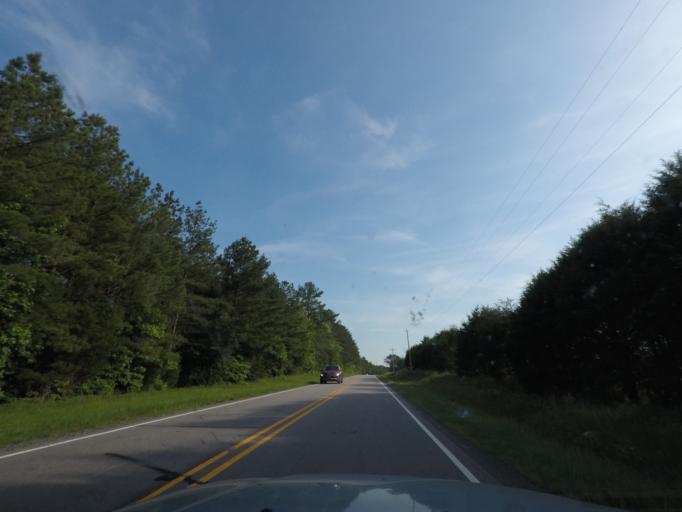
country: US
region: Virginia
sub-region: Mecklenburg County
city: Clarksville
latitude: 36.4746
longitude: -78.5552
